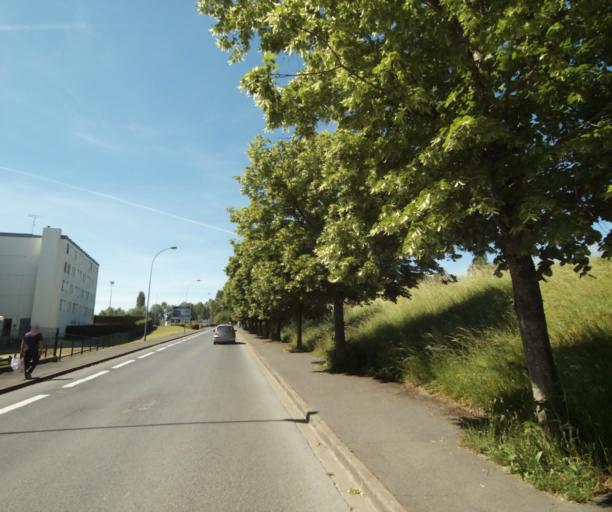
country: FR
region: Champagne-Ardenne
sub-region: Departement des Ardennes
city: Villers-Semeuse
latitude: 49.7477
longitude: 4.7292
